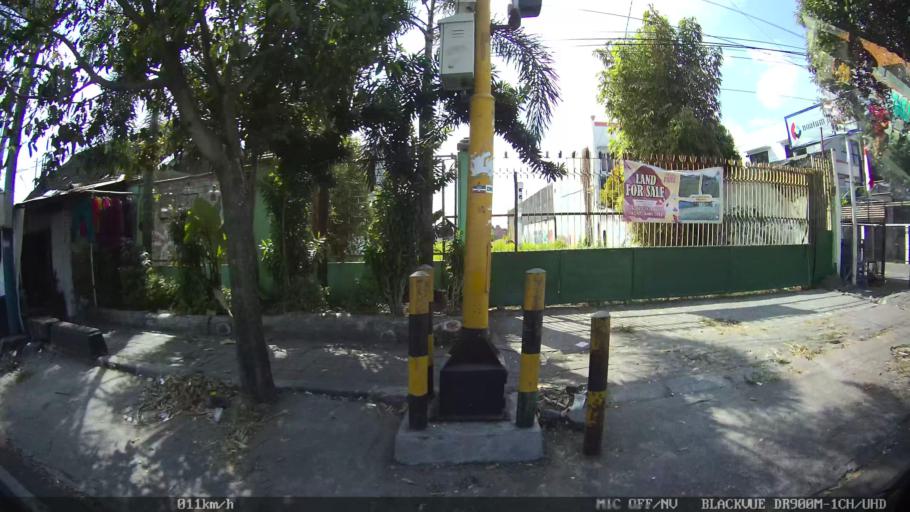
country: ID
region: Daerah Istimewa Yogyakarta
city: Kasihan
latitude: -7.8246
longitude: 110.3678
